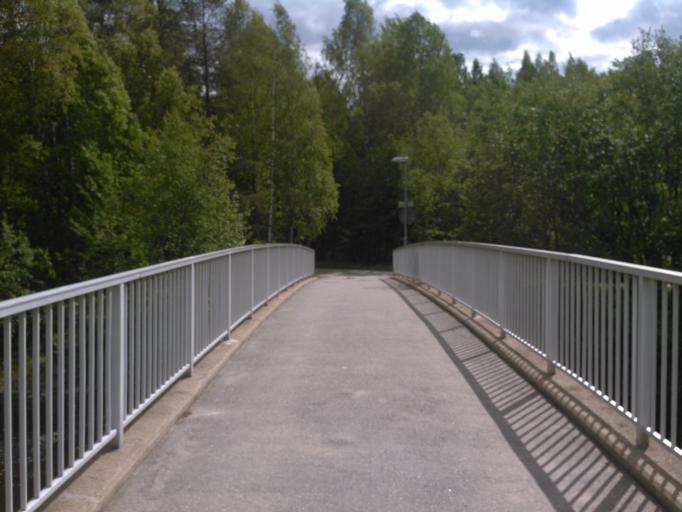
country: SE
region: Vaesterbotten
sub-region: Umea Kommun
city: Umea
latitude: 63.8250
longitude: 20.2216
